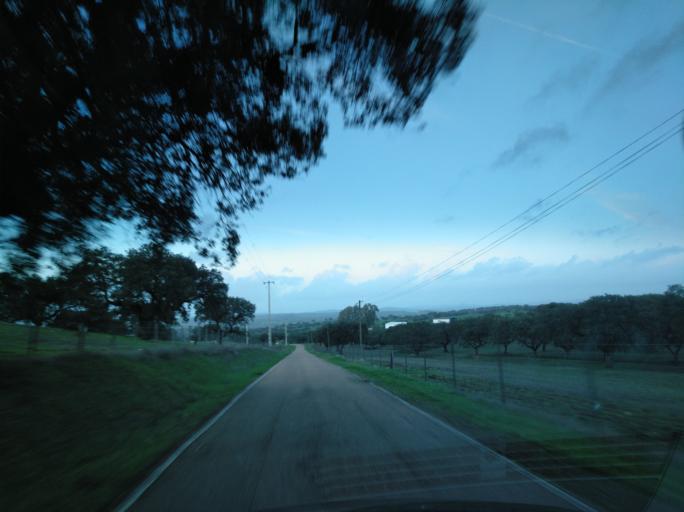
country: PT
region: Portalegre
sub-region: Campo Maior
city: Campo Maior
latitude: 39.0718
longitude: -7.1155
